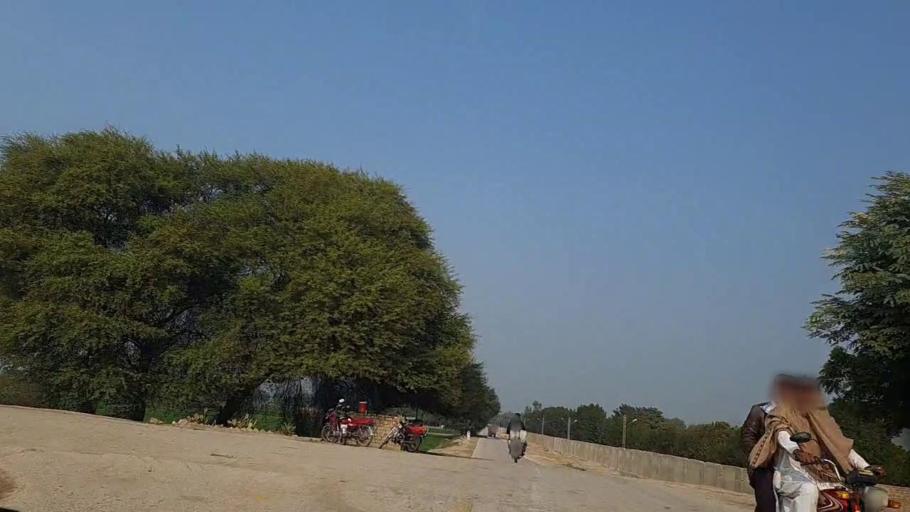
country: PK
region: Sindh
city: Sann
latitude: 26.1778
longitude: 68.1078
